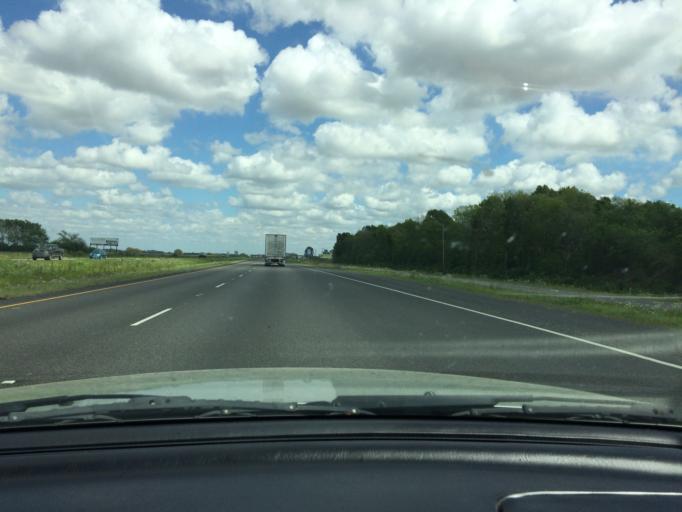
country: US
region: Louisiana
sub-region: Jefferson Davis Parish
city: Jennings
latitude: 30.2474
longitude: -92.7351
